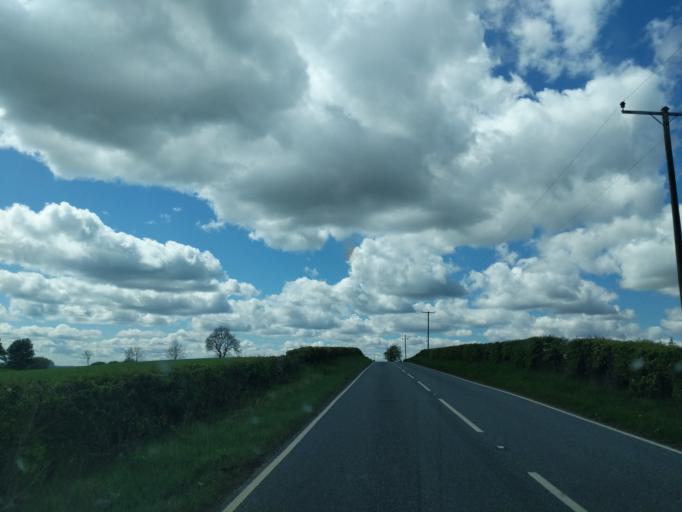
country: GB
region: Scotland
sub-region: Stirling
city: Doune
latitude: 56.1675
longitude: -4.1057
